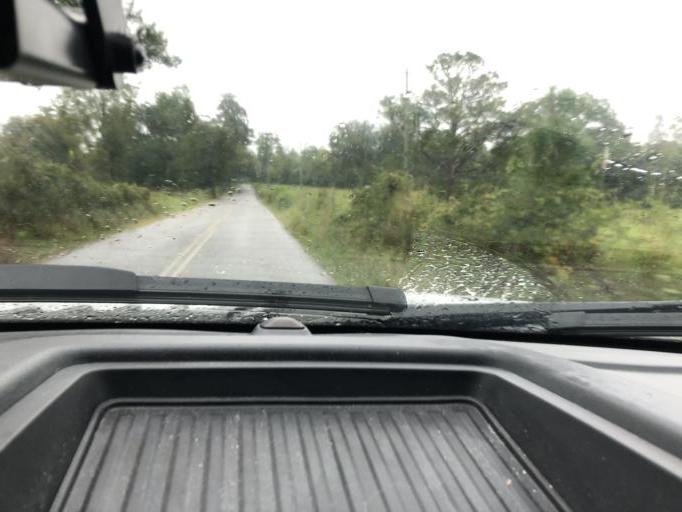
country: US
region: Georgia
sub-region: Putnam County
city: Jefferson
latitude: 33.3896
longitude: -83.2538
